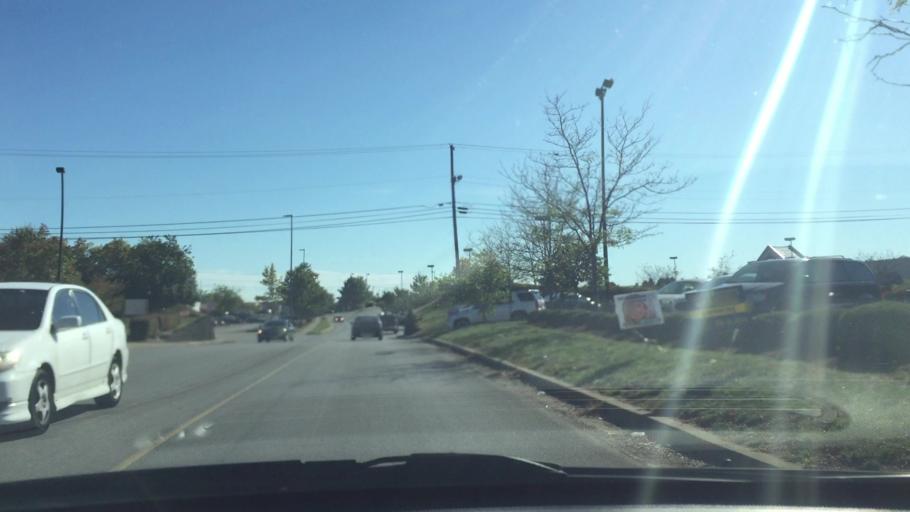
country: US
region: Kentucky
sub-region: Fayette County
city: Monticello
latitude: 37.9811
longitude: -84.5322
